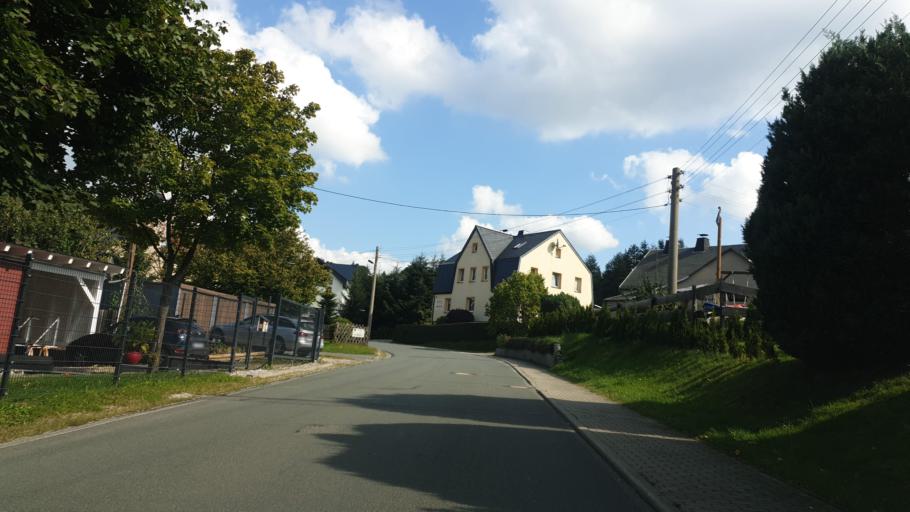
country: DE
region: Saxony
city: Rodewisch
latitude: 50.5074
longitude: 12.4581
